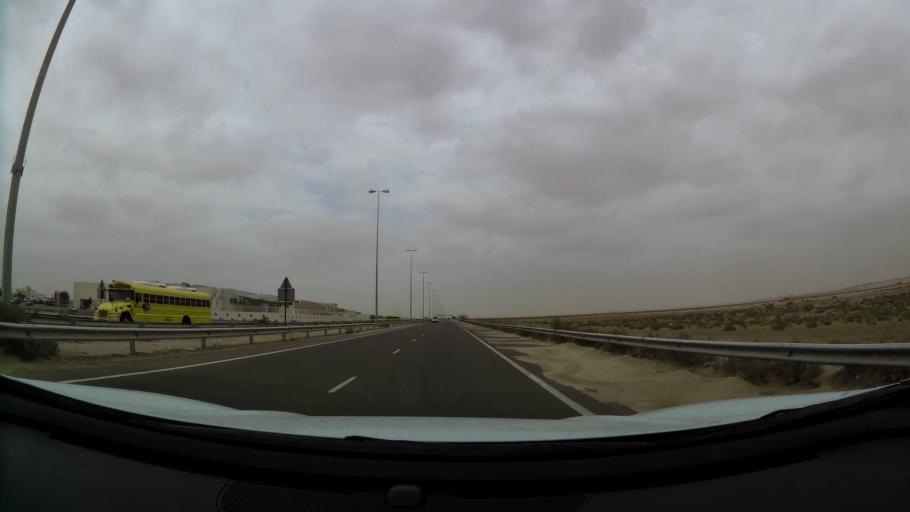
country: AE
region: Abu Dhabi
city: Abu Dhabi
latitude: 24.3247
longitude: 54.6432
